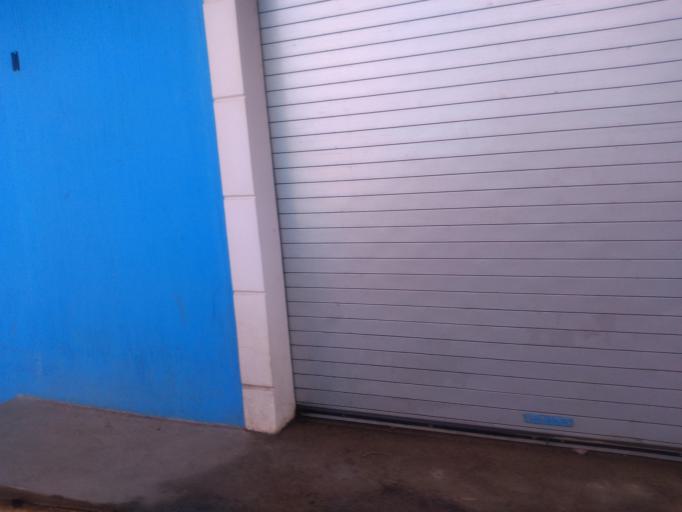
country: GT
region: Quetzaltenango
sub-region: Municipio de La Esperanza
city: La Esperanza
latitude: 14.8585
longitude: -91.5701
